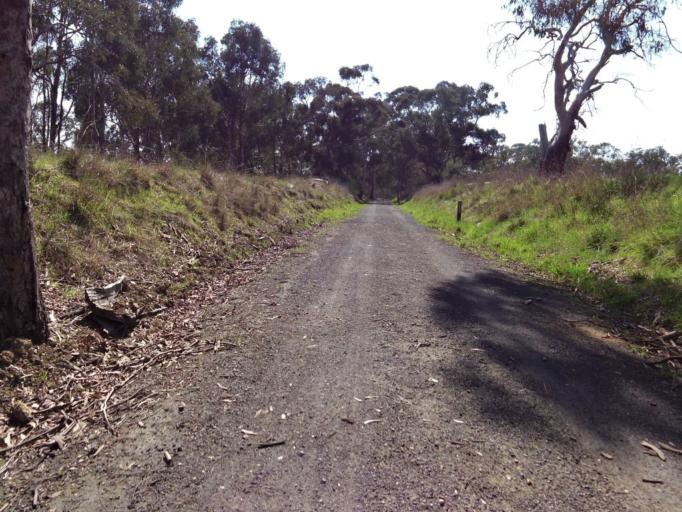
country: AU
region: Victoria
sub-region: Murrindindi
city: Alexandra
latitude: -37.1205
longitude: 145.6026
